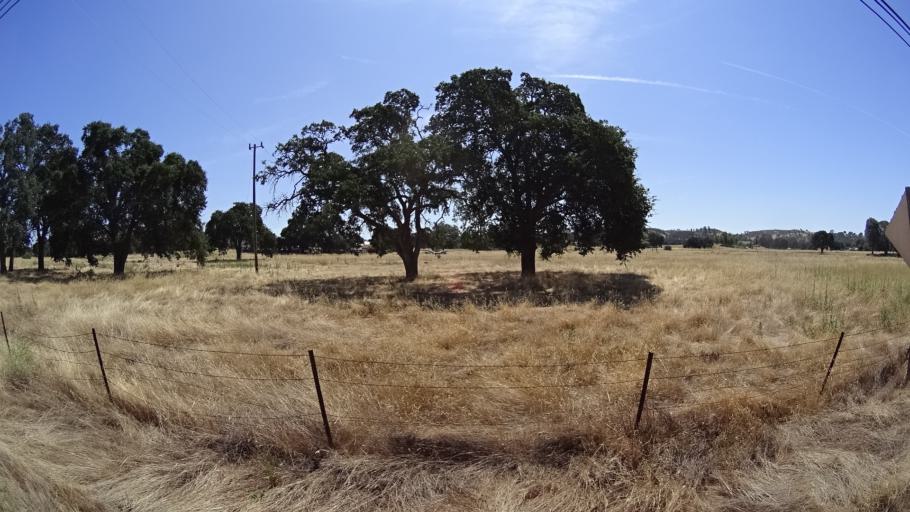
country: US
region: California
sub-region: Calaveras County
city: Valley Springs
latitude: 38.1816
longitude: -120.8905
